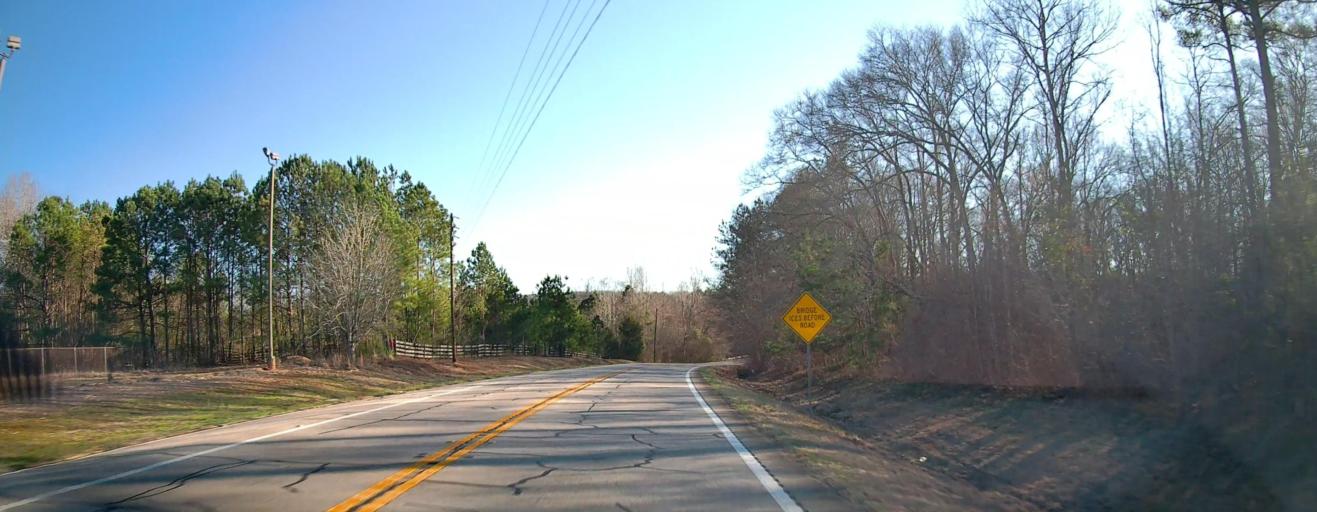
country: US
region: Georgia
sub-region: Meriwether County
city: Manchester
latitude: 32.8742
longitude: -84.5971
